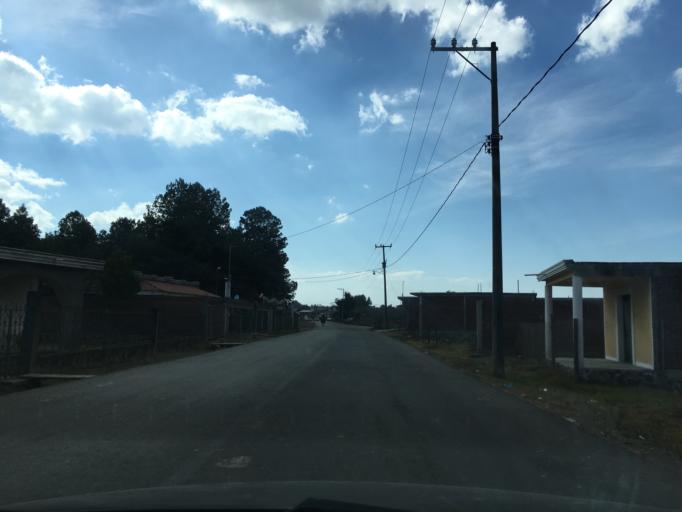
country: MX
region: Michoacan
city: Angahuan
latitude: 19.5479
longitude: -102.2176
